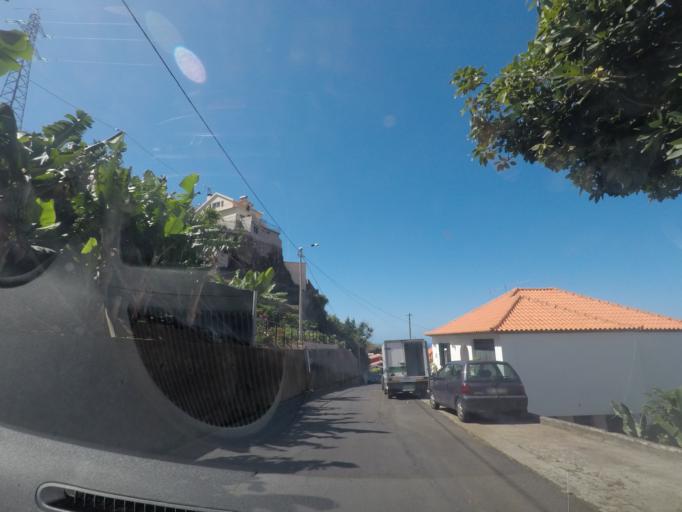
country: PT
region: Madeira
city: Ponta do Sol
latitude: 32.6866
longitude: -17.0917
